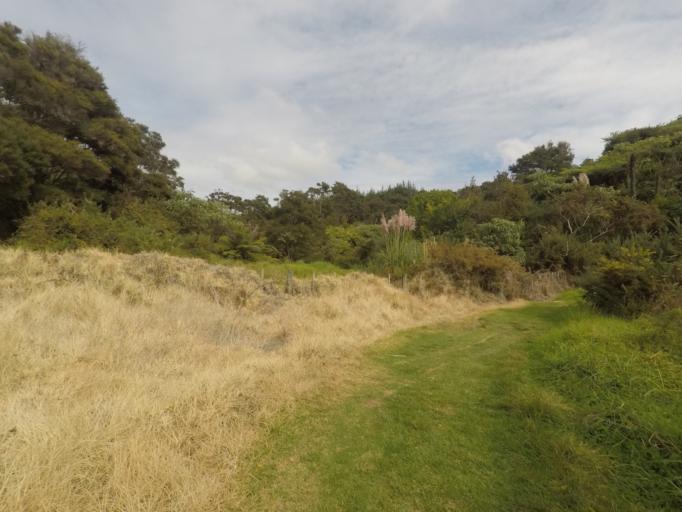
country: NZ
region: Auckland
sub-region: Auckland
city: Rothesay Bay
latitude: -36.6441
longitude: 174.7221
